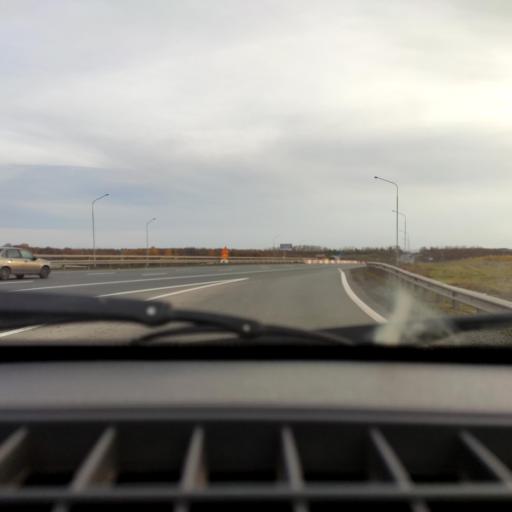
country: RU
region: Bashkortostan
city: Avdon
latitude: 54.6655
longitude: 55.7386
